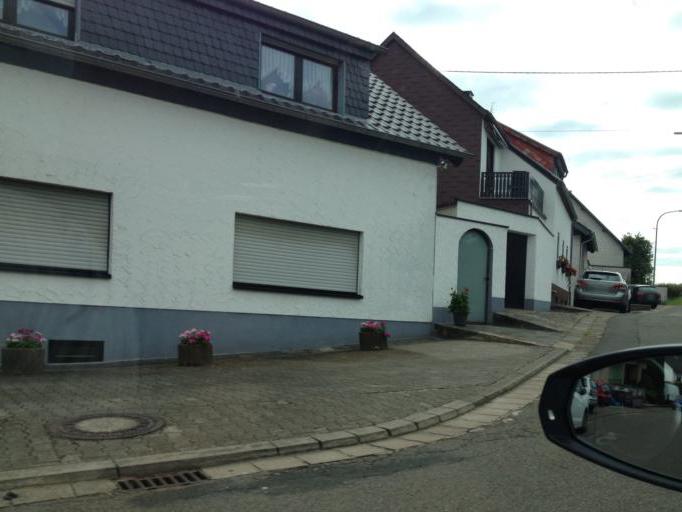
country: DE
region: Saarland
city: Eppelborn
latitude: 49.4583
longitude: 6.9547
